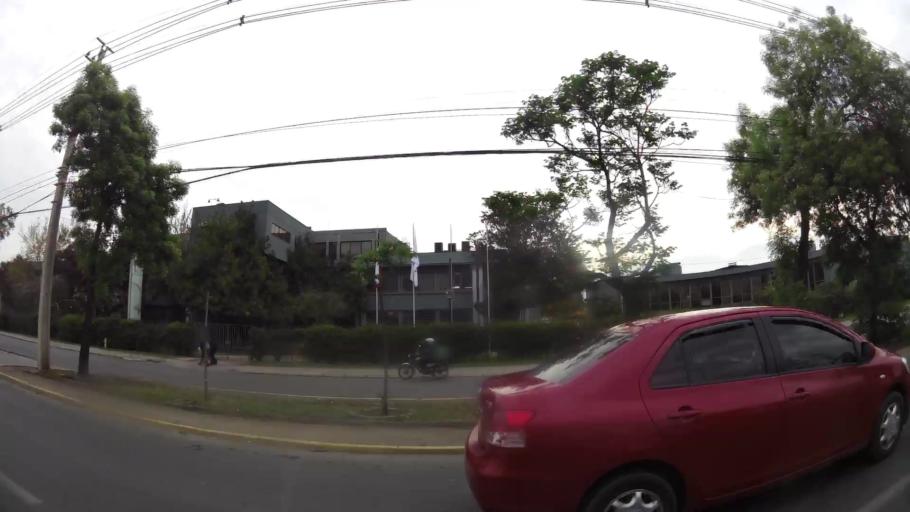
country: CL
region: Santiago Metropolitan
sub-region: Provincia de Santiago
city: Santiago
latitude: -33.4647
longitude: -70.6149
